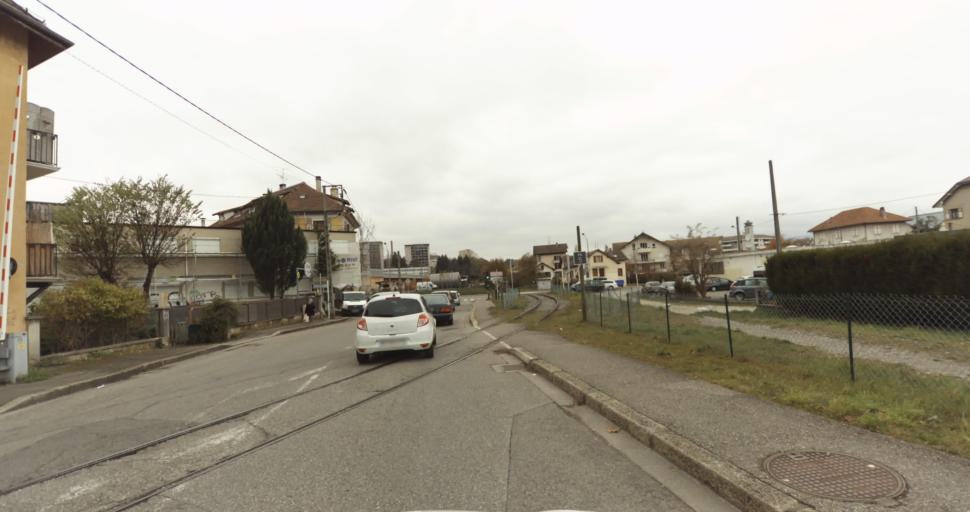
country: FR
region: Rhone-Alpes
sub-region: Departement de la Haute-Savoie
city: Annecy
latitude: 45.8925
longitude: 6.1181
